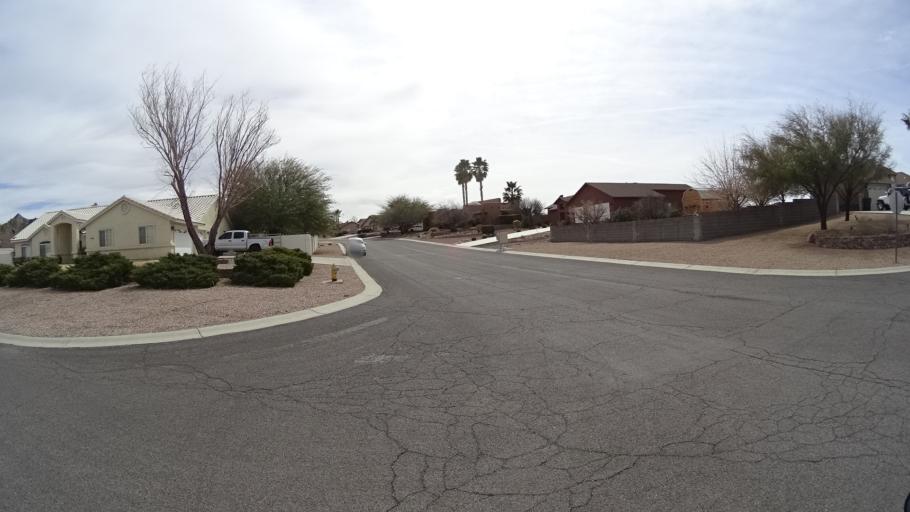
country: US
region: Arizona
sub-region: Mohave County
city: Kingman
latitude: 35.1953
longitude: -113.9798
